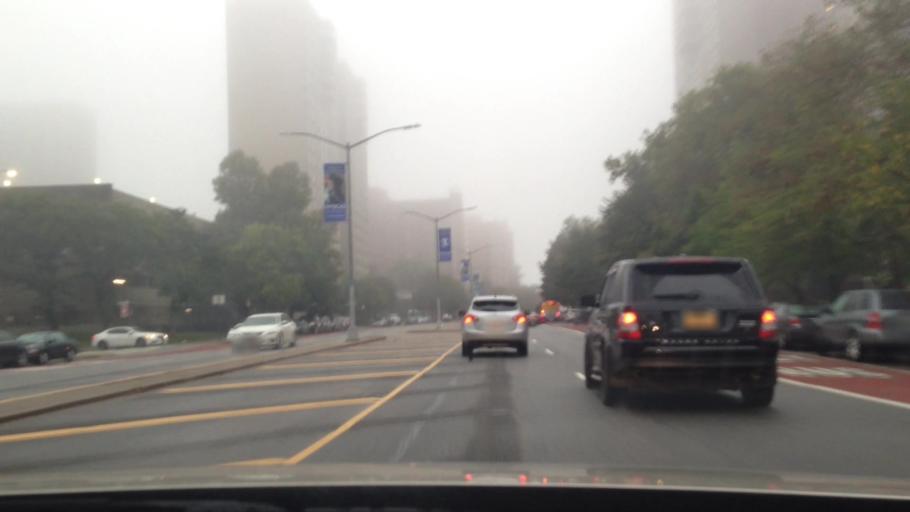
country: US
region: New York
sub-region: Kings County
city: East New York
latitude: 40.6490
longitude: -73.8831
